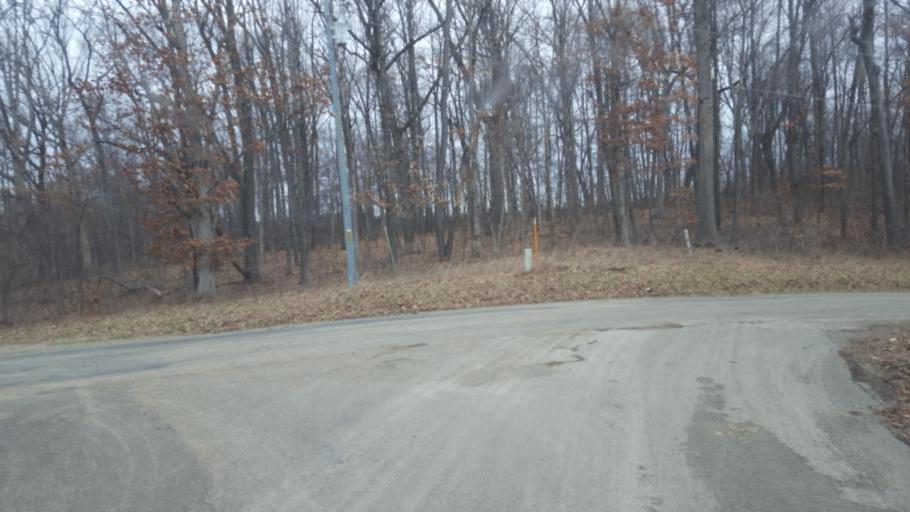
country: US
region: Ohio
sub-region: Sandusky County
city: Bellville
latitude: 40.5725
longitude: -82.3806
